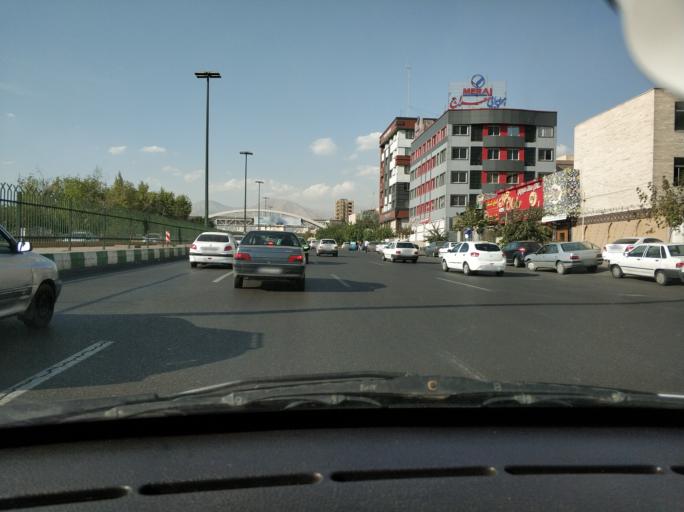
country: IR
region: Tehran
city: Tehran
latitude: 35.7042
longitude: 51.3376
